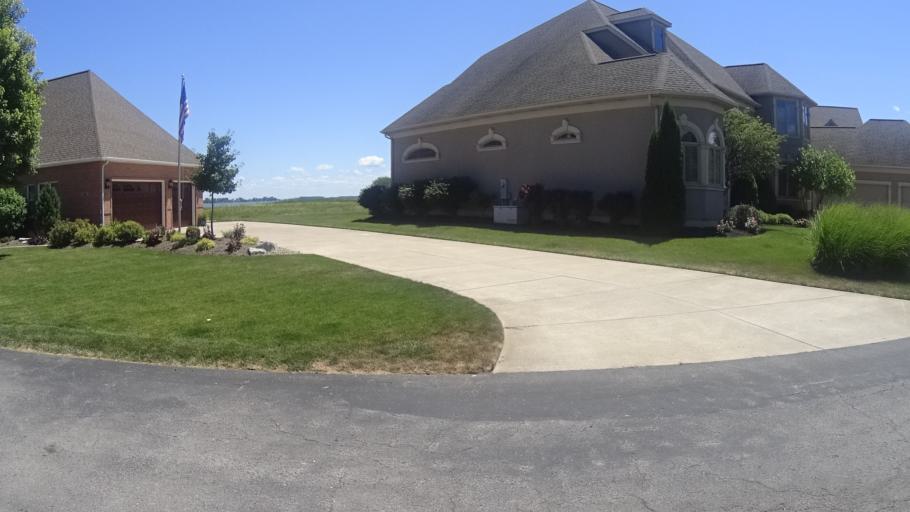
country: US
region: Ohio
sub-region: Erie County
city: Sandusky
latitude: 41.4452
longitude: -82.6711
